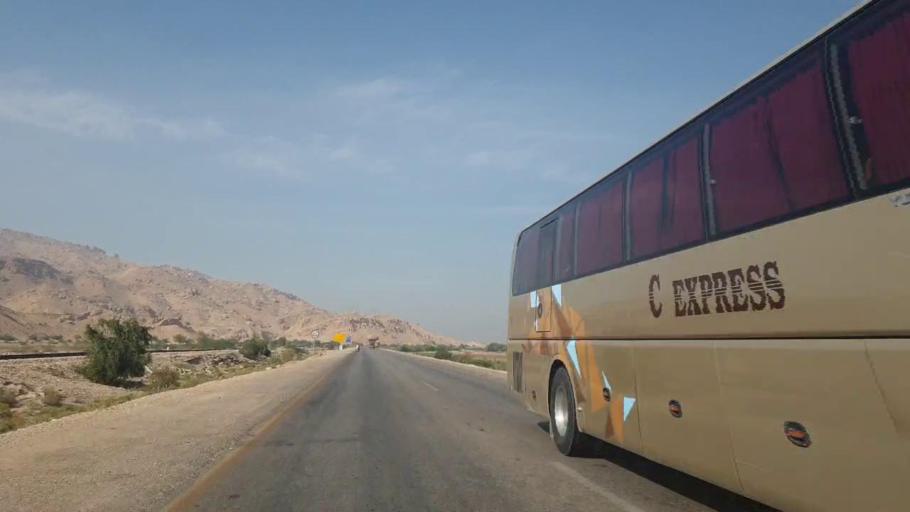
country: PK
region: Sindh
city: Sehwan
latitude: 26.2829
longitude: 67.8956
